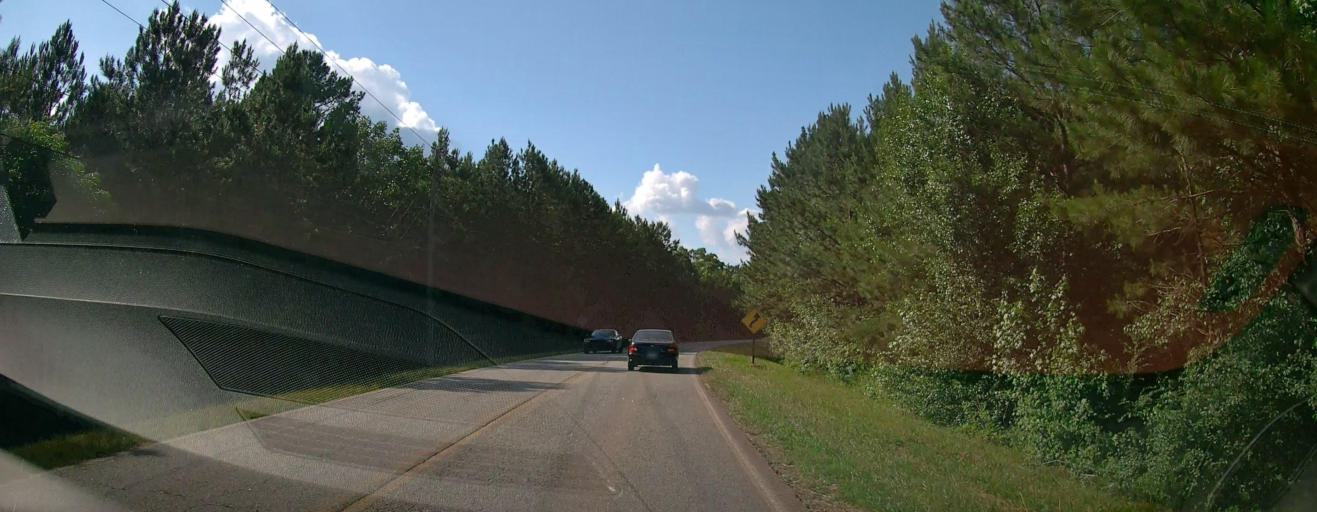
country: US
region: Georgia
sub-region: Henry County
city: McDonough
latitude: 33.4440
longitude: -84.2132
